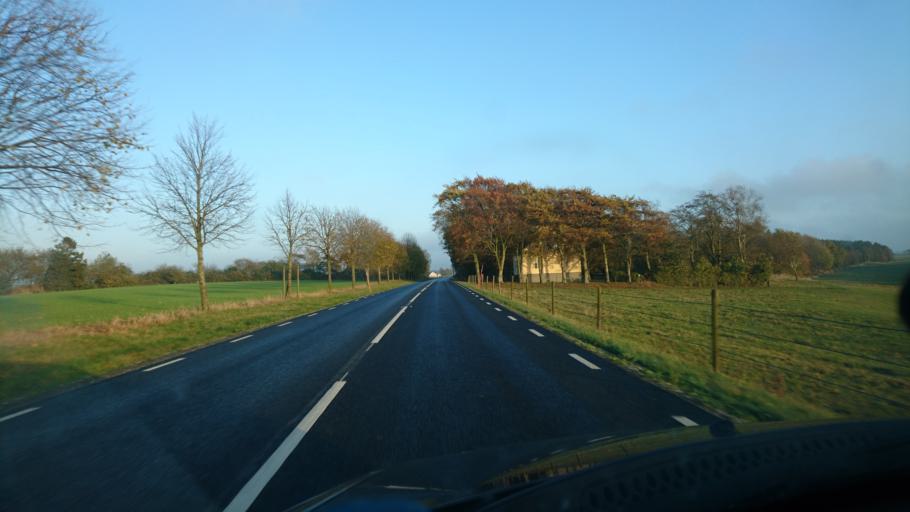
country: SE
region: Skane
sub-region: Tomelilla Kommun
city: Tomelilla
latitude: 55.4919
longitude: 14.0589
